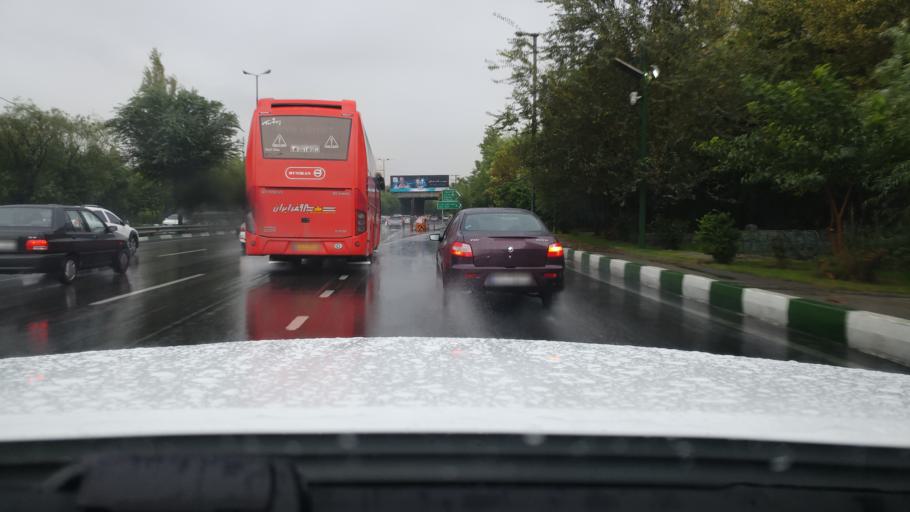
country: IR
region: Tehran
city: Tehran
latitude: 35.7444
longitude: 51.4218
